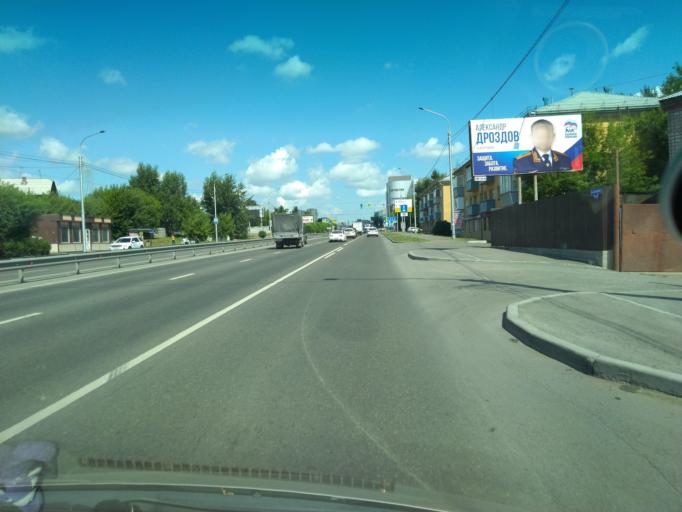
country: RU
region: Krasnoyarskiy
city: Krasnoyarsk
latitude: 56.0262
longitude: 92.8872
